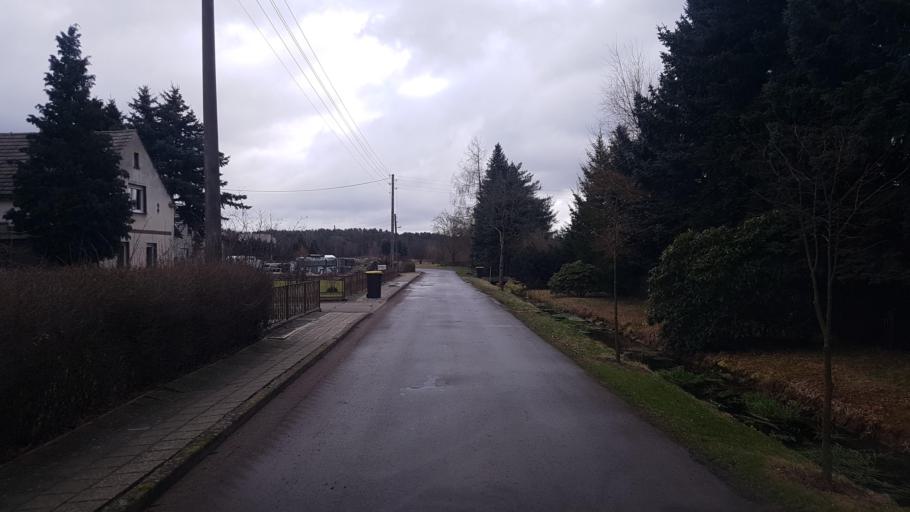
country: DE
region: Brandenburg
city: Kroppen
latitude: 51.3787
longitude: 13.7991
